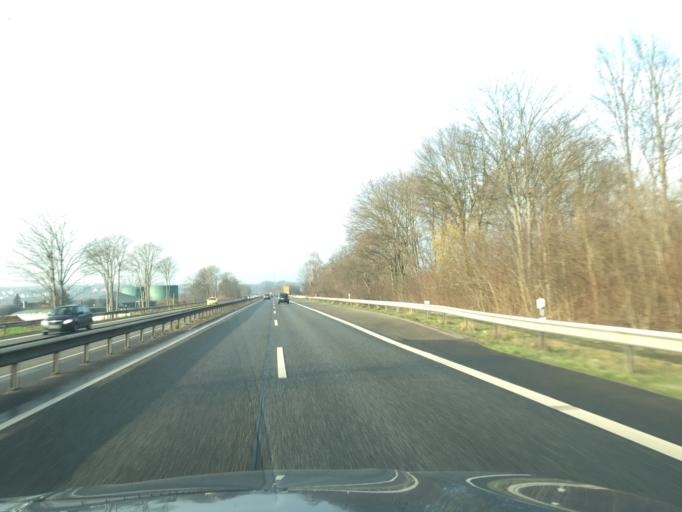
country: DE
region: Rheinland-Pfalz
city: Kettig
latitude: 50.4028
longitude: 7.4869
